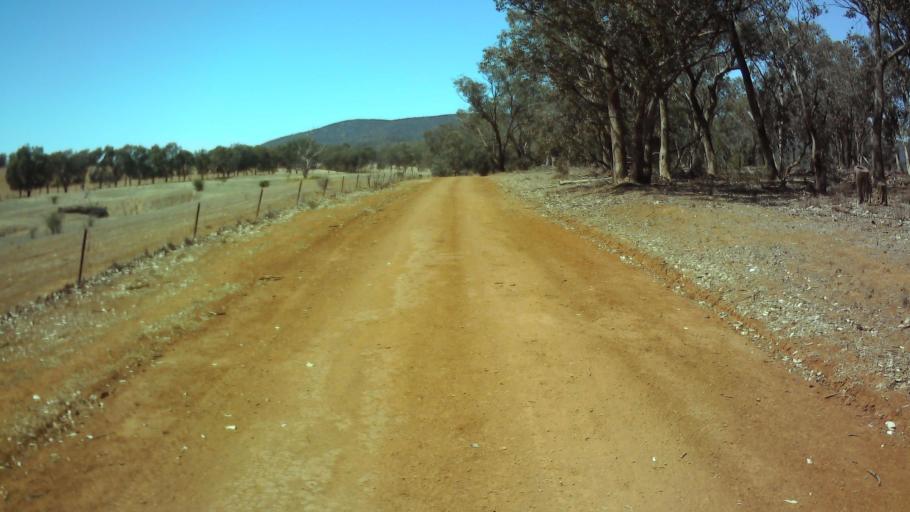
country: AU
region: New South Wales
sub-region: Weddin
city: Grenfell
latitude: -33.9514
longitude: 148.0846
